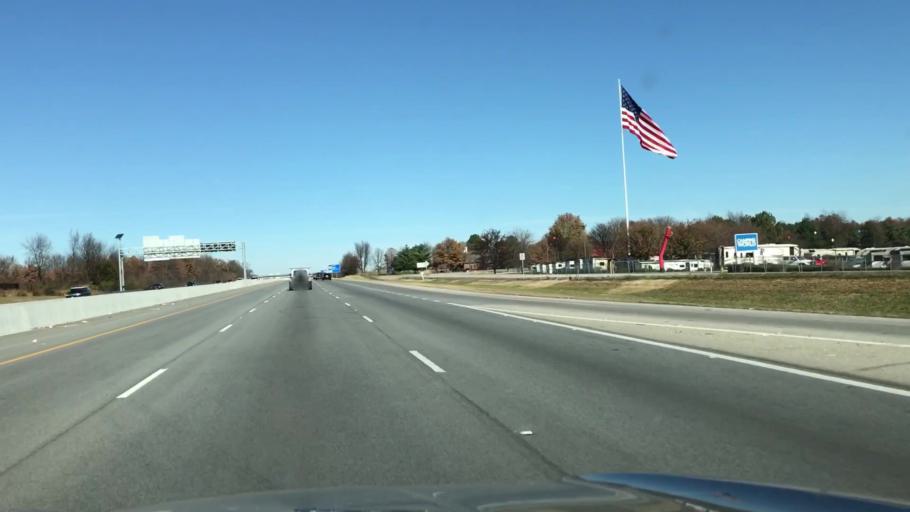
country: US
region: Arkansas
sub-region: Benton County
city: Lowell
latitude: 36.2582
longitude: -94.1503
